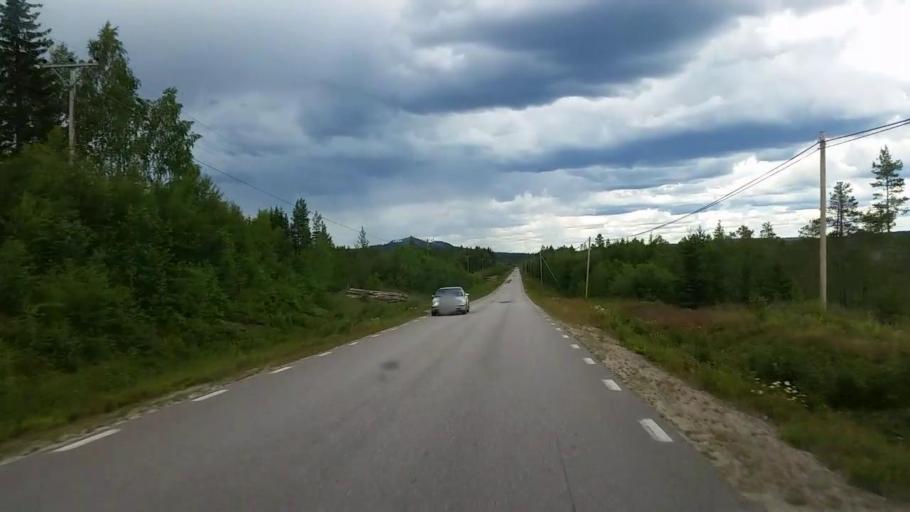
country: SE
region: Gaevleborg
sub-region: Ovanakers Kommun
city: Edsbyn
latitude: 61.4393
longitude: 15.8919
